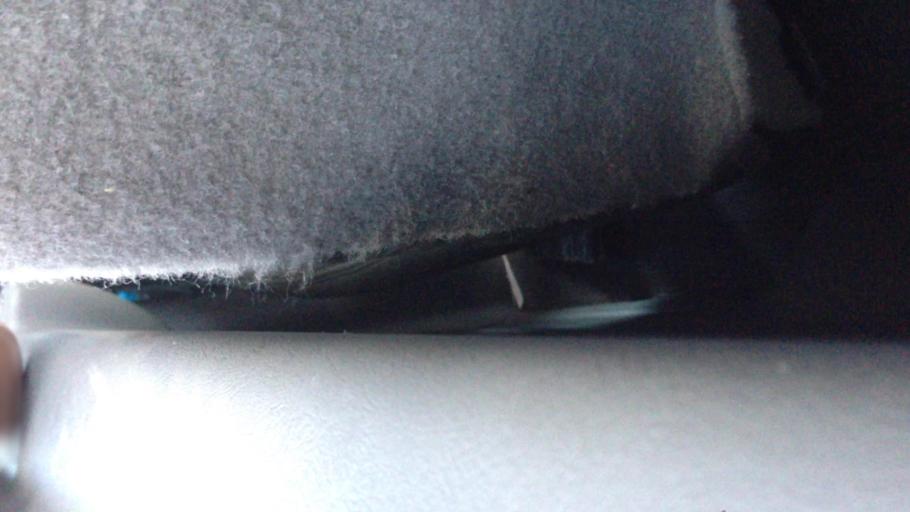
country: US
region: New York
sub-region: Columbia County
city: Oakdale
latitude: 42.2549
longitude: -73.7789
